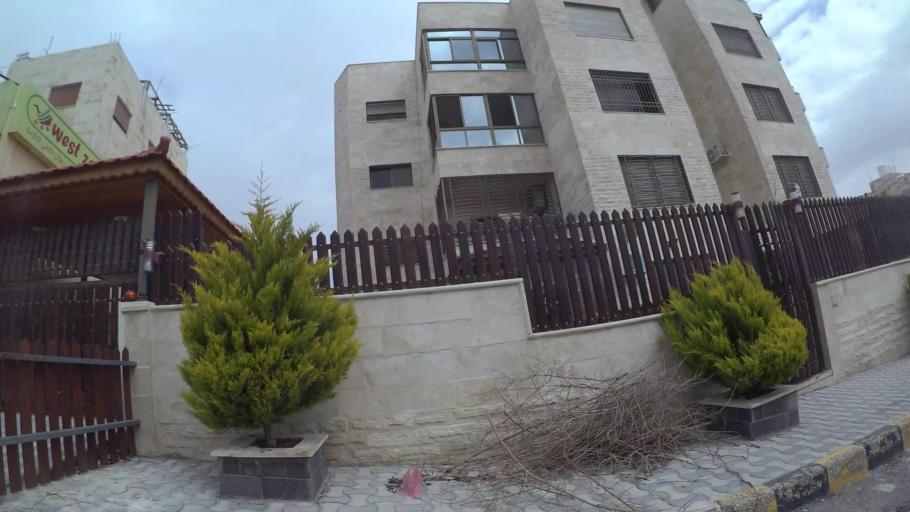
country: JO
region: Amman
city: Umm as Summaq
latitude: 31.9025
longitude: 35.8442
